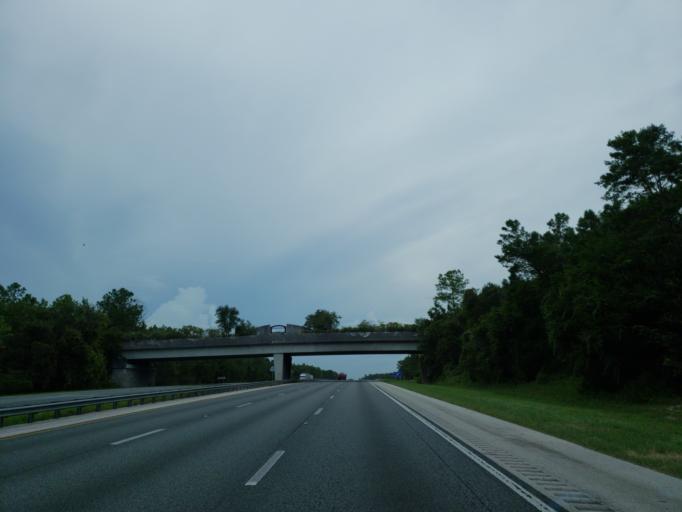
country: US
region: Florida
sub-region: Marion County
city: Belleview
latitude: 29.0346
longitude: -82.1627
